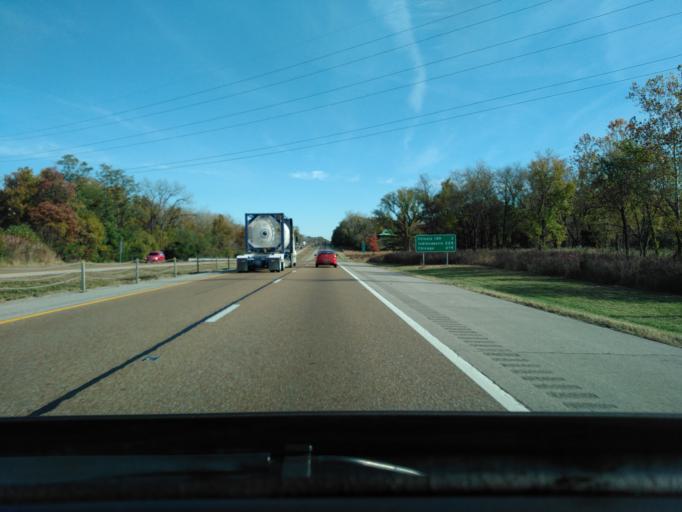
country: US
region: Illinois
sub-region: Madison County
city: Collinsville
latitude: 38.6884
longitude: -90.0033
